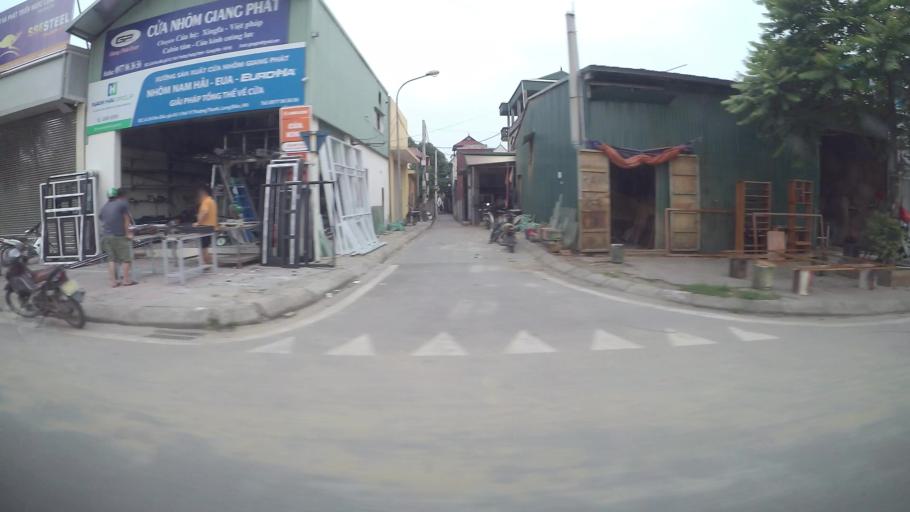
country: VN
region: Ha Noi
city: Hoan Kiem
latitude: 21.0733
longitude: 105.8889
